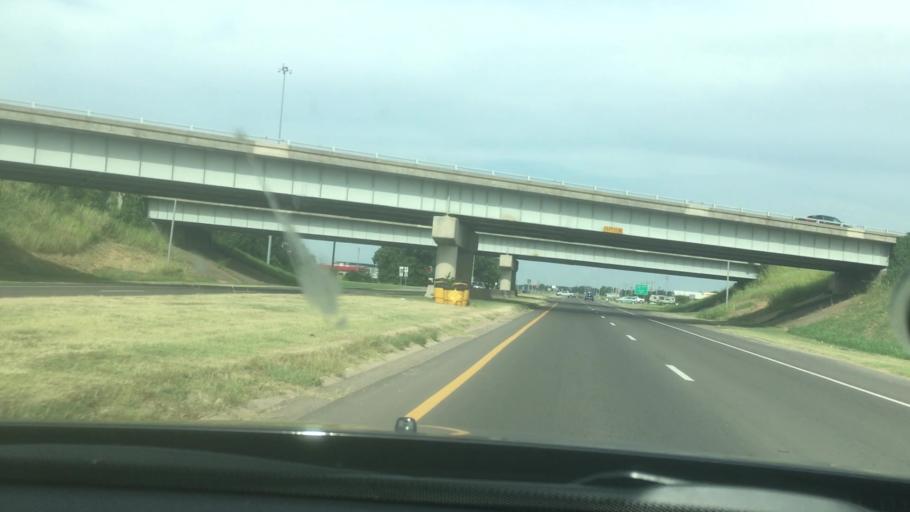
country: US
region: Oklahoma
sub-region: Garvin County
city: Pauls Valley
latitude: 34.7395
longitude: -97.2621
